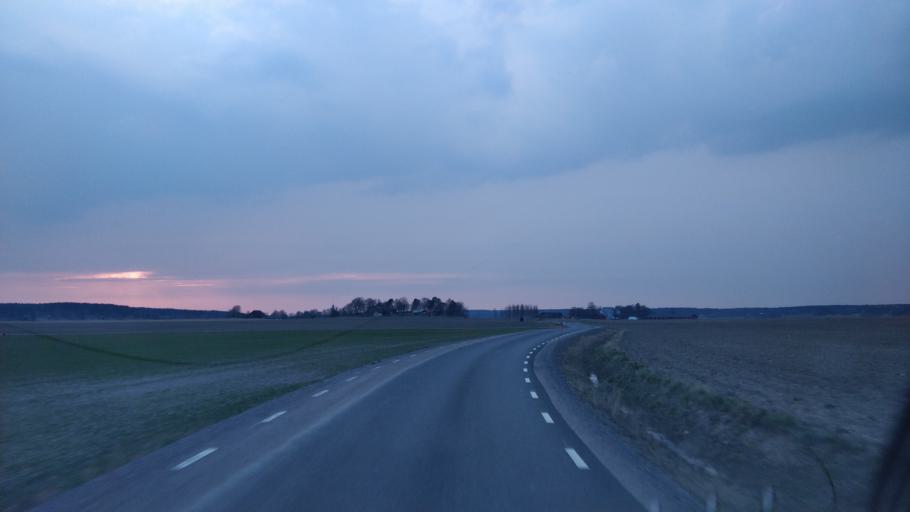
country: SE
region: Uppsala
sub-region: Enkopings Kommun
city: Orsundsbro
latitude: 59.7257
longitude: 17.2190
